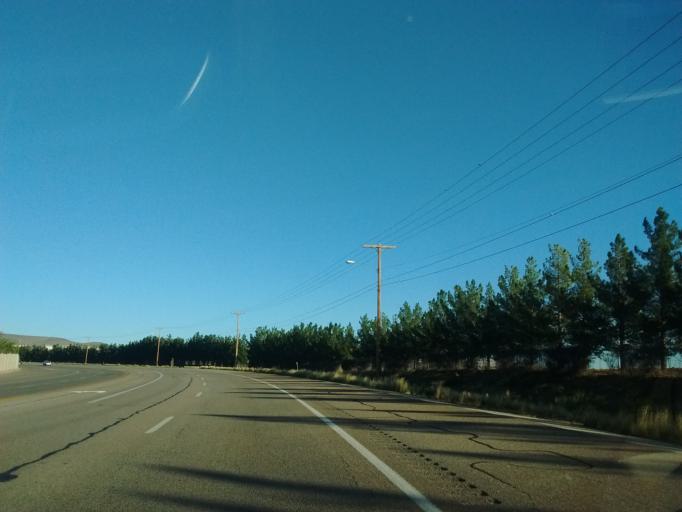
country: US
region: Utah
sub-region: Washington County
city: Hurricane
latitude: 37.1620
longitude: -113.3942
